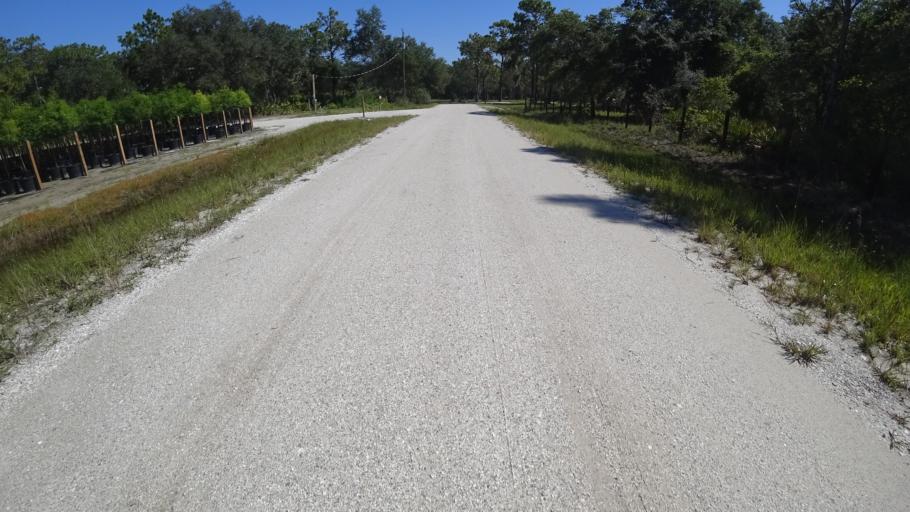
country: US
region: Florida
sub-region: Sarasota County
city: The Meadows
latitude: 27.4122
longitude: -82.2956
